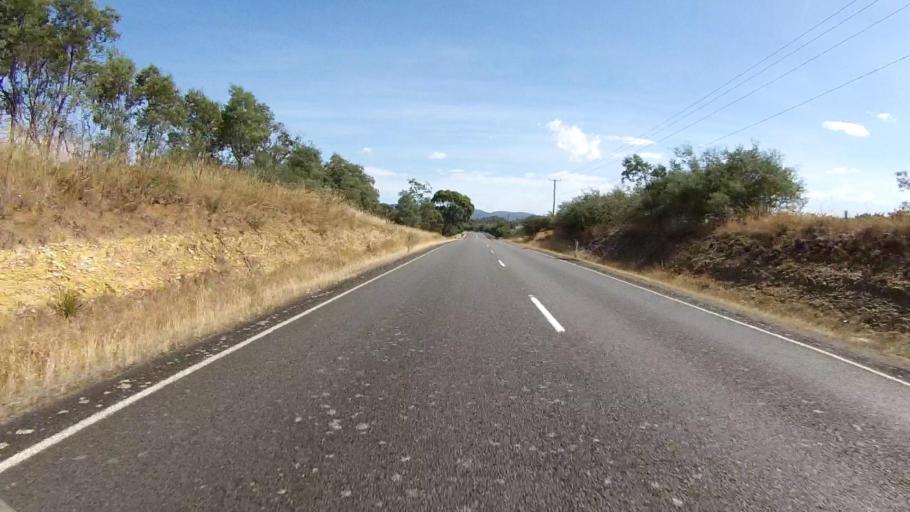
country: AU
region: Tasmania
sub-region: Sorell
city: Sorell
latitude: -42.5931
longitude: 147.7933
